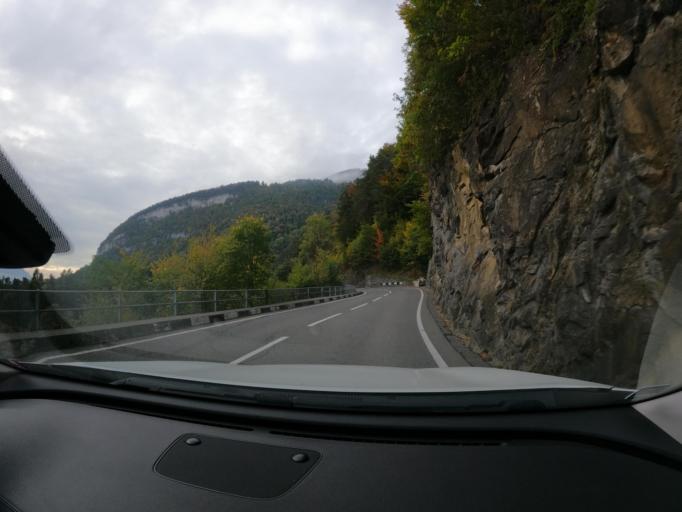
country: CH
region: Bern
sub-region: Interlaken-Oberhasli District
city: Beatenberg
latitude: 46.6856
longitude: 7.8014
